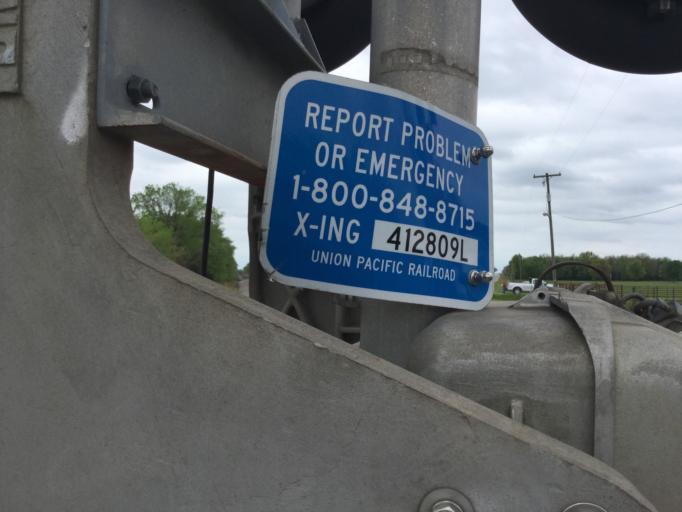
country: US
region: Kansas
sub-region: Labette County
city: Parsons
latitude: 37.3094
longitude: -95.2496
